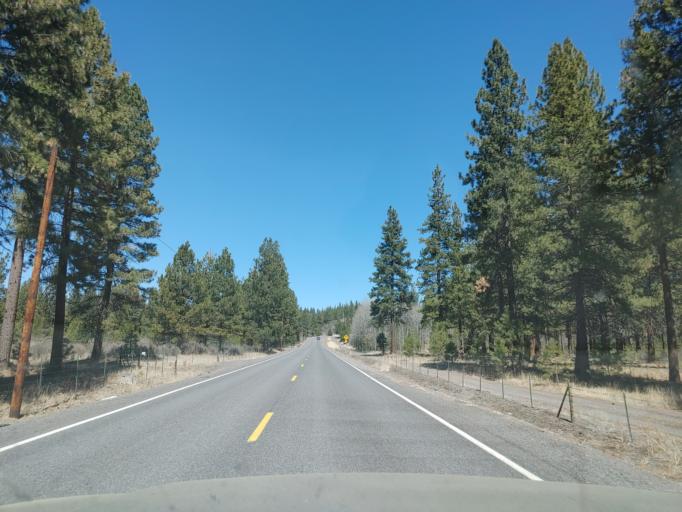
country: US
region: Oregon
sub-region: Klamath County
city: Klamath Falls
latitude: 42.5545
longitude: -121.8949
